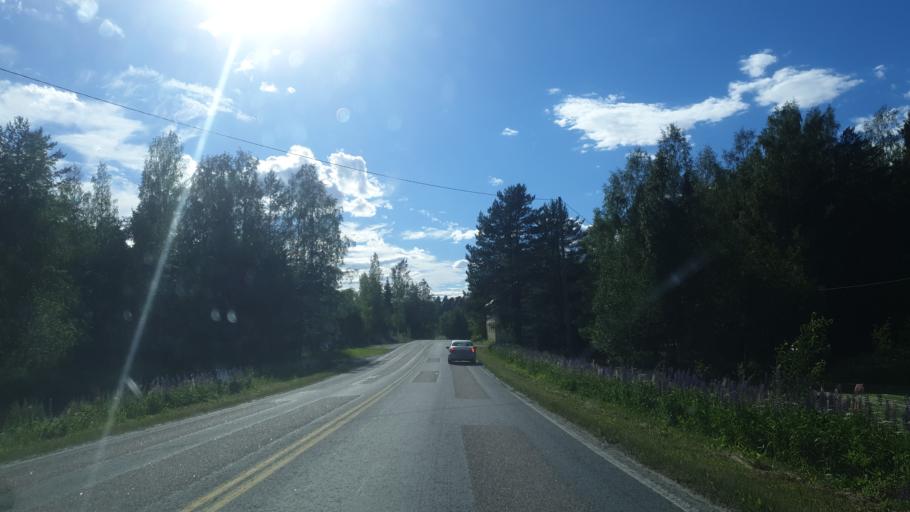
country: FI
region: Southern Savonia
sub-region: Mikkeli
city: Pertunmaa
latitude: 61.5231
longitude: 26.5502
